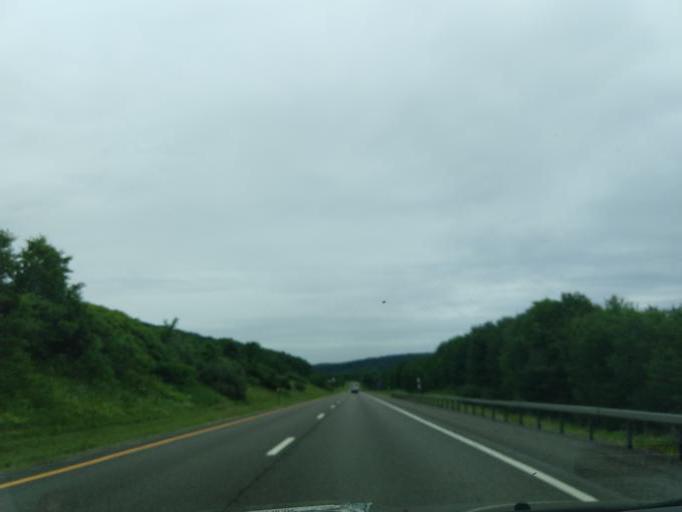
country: US
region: New York
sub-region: Broome County
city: Chenango Bridge
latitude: 42.1956
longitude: -75.8997
